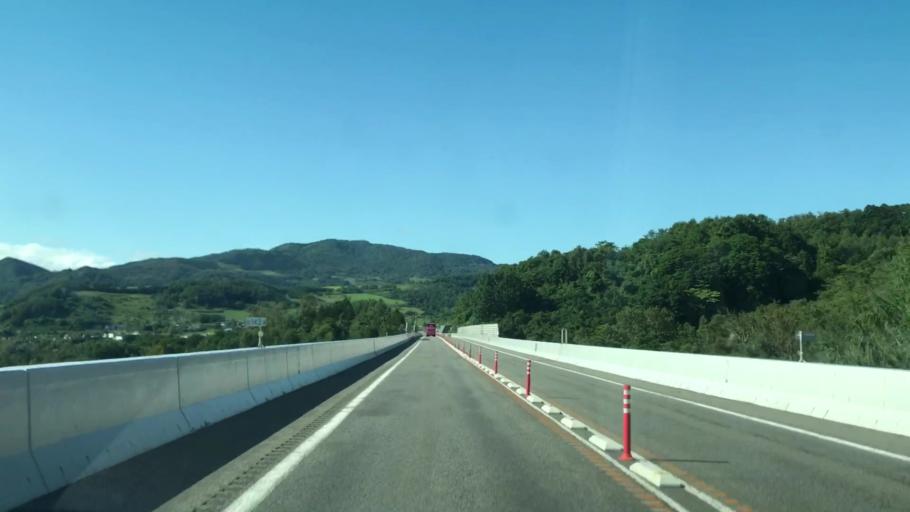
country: JP
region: Hokkaido
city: Date
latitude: 42.5374
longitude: 140.7969
